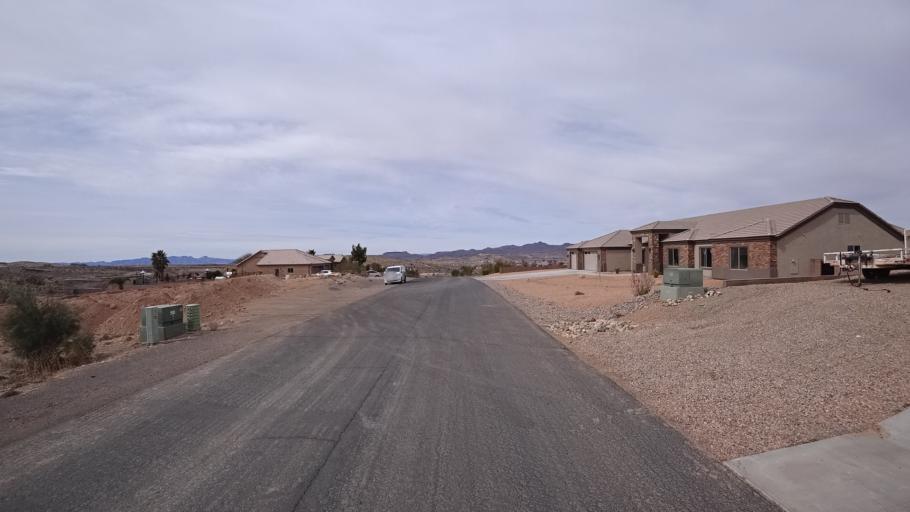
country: US
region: Arizona
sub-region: Mohave County
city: Kingman
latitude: 35.1783
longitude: -113.9983
